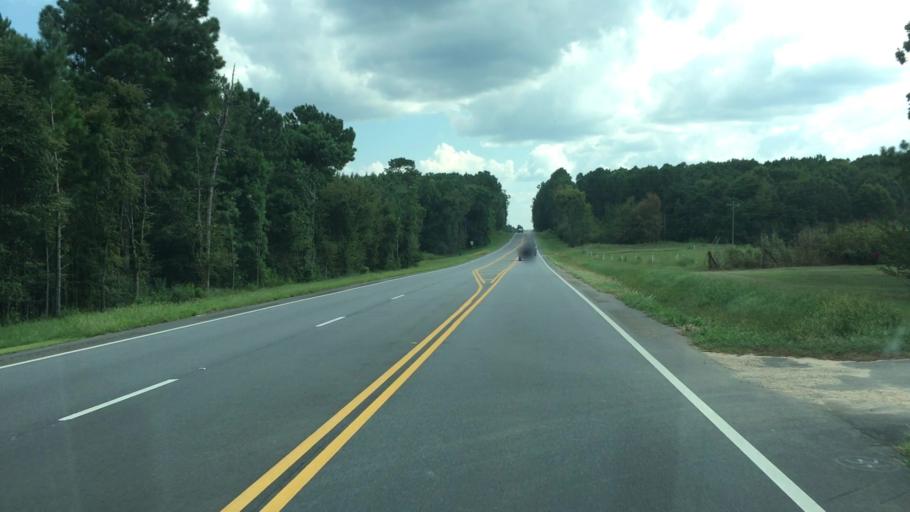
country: US
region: Georgia
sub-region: Putnam County
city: Jefferson
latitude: 33.4652
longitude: -83.4147
